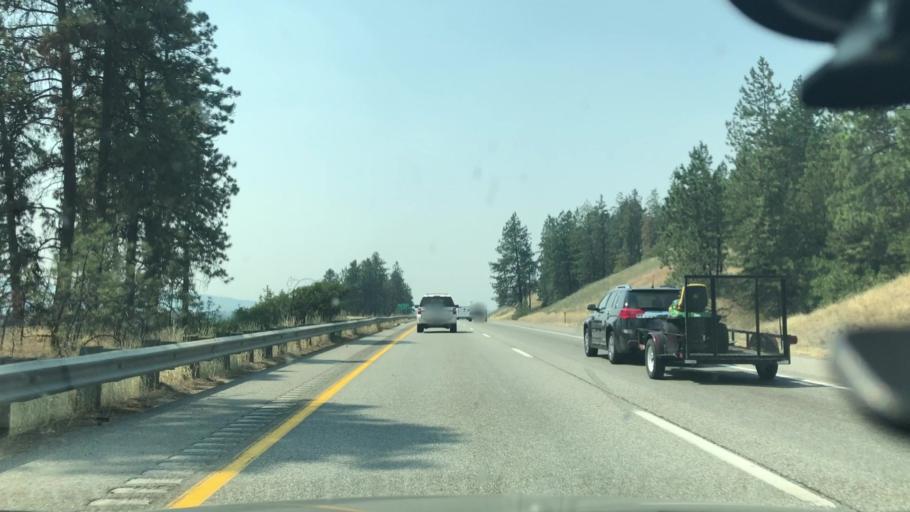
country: US
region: Idaho
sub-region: Kootenai County
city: Post Falls
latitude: 47.7093
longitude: -116.8813
